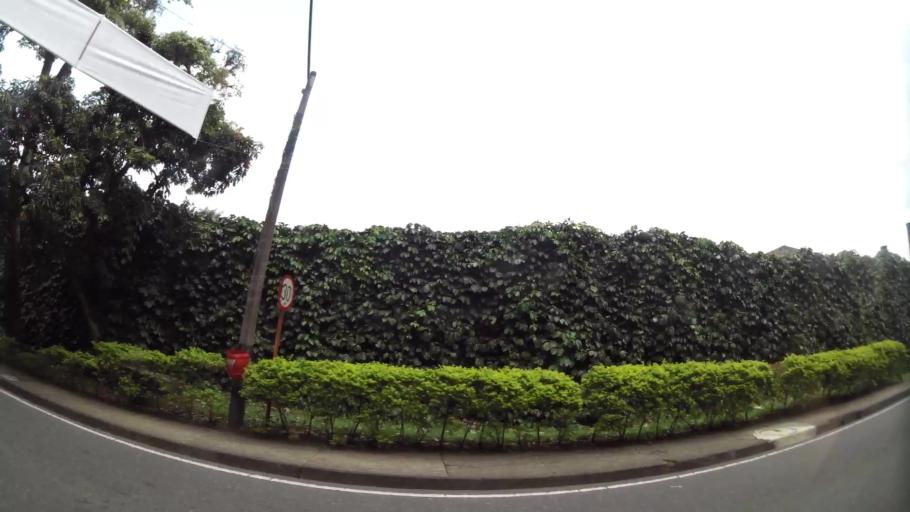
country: CO
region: Antioquia
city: Envigado
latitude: 6.1894
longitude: -75.5761
